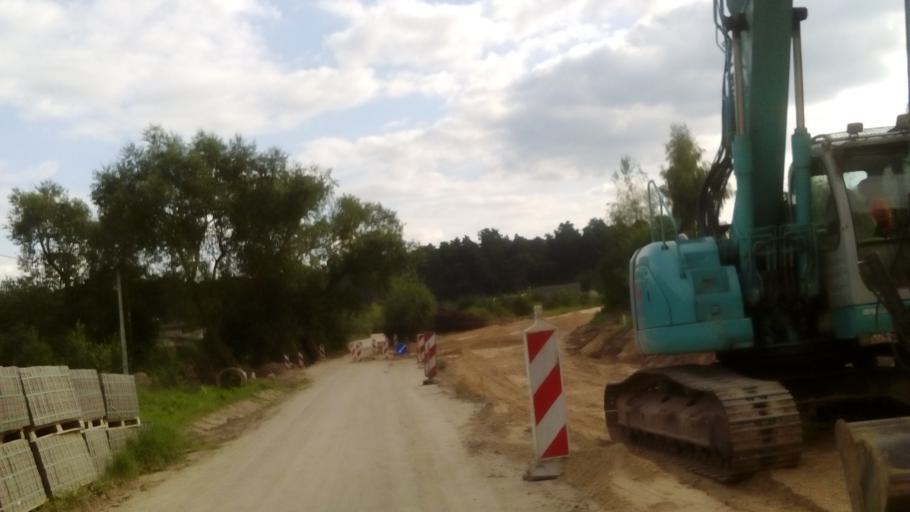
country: LT
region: Alytaus apskritis
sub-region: Alytus
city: Alytus
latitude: 54.4195
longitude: 24.0374
